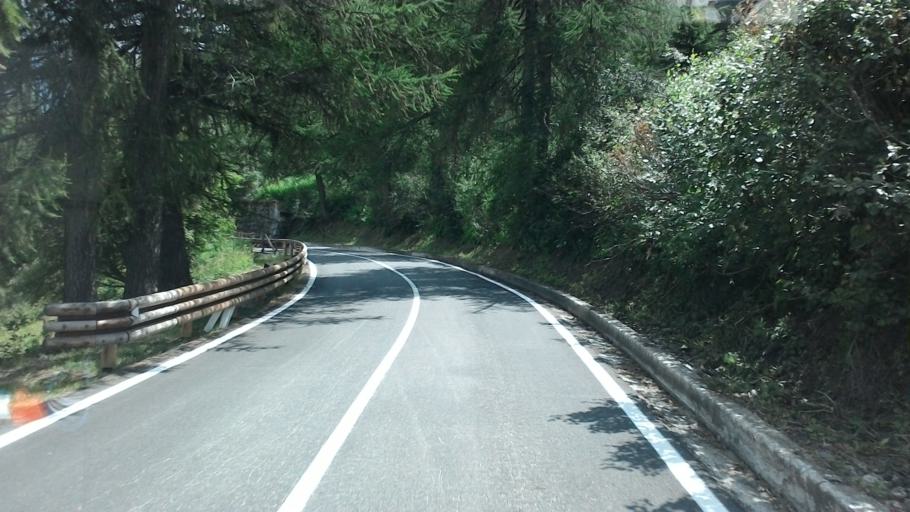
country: IT
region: Aosta Valley
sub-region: Valle d'Aosta
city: La Thuile
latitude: 45.7081
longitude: 6.9312
